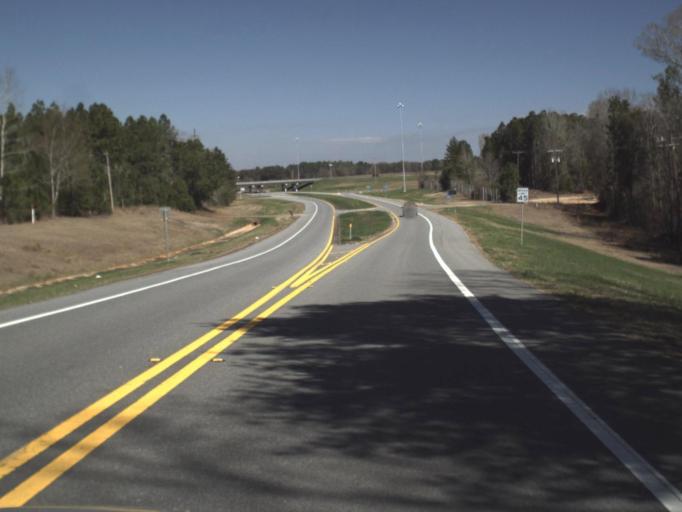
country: US
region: Florida
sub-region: Jackson County
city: Sneads
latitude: 30.6516
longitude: -85.0392
